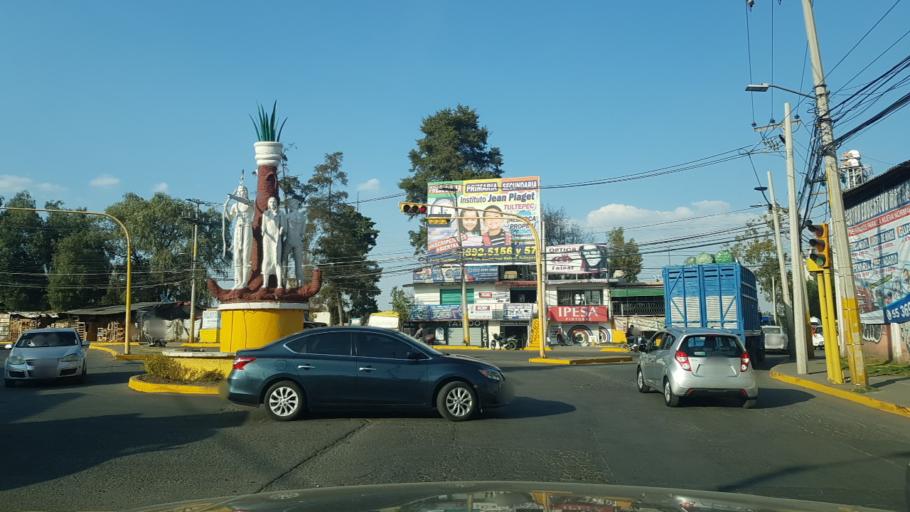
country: MX
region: Mexico
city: Santiago Teyahualco
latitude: 19.6612
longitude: -99.1268
